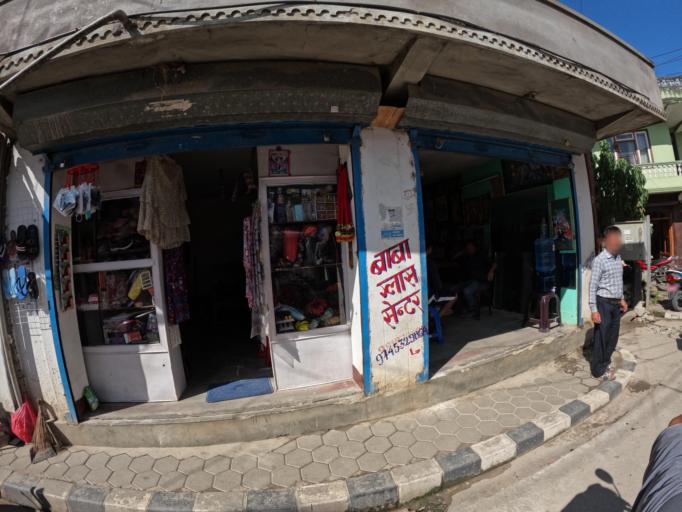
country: NP
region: Central Region
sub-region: Bagmati Zone
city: Kathmandu
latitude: 27.7506
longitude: 85.3365
